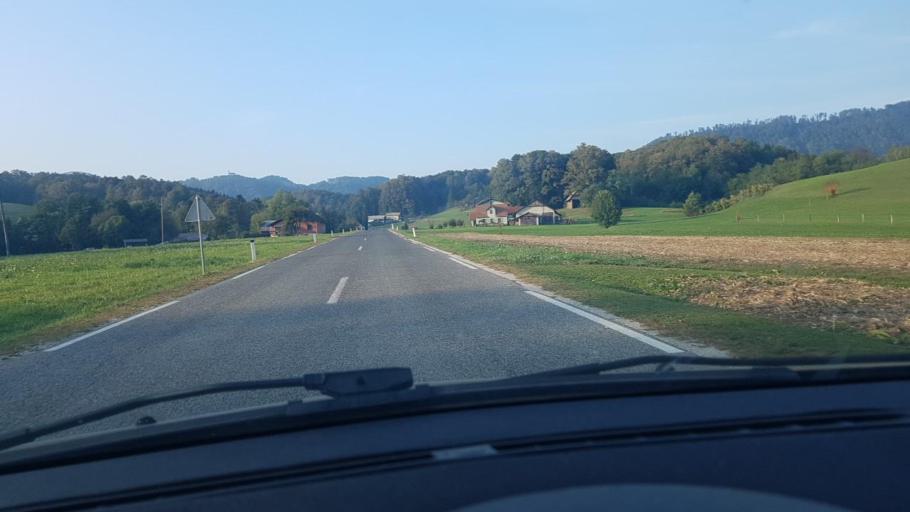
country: SI
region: Rogatec
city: Rogatec
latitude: 46.2414
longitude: 15.7017
